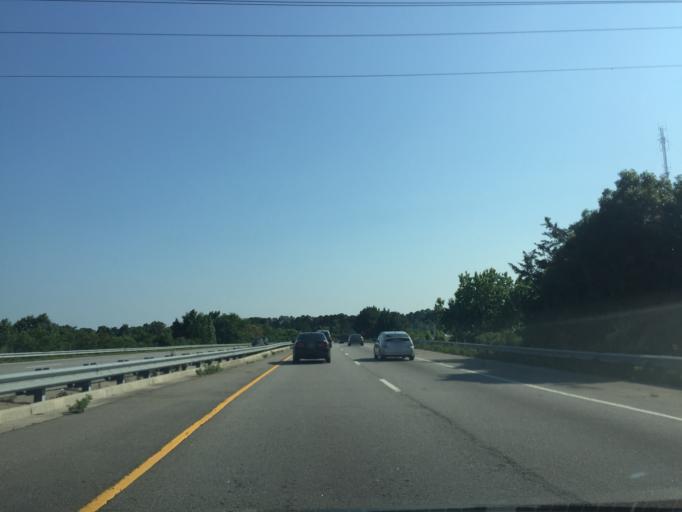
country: US
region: Georgia
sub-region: Chatham County
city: Thunderbolt
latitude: 32.0435
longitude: -81.0698
